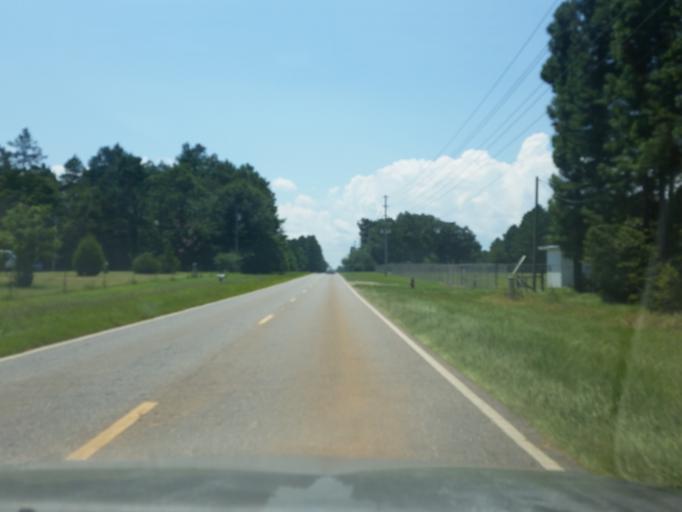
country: US
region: Alabama
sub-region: Baldwin County
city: Robertsdale
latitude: 30.6260
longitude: -87.6519
